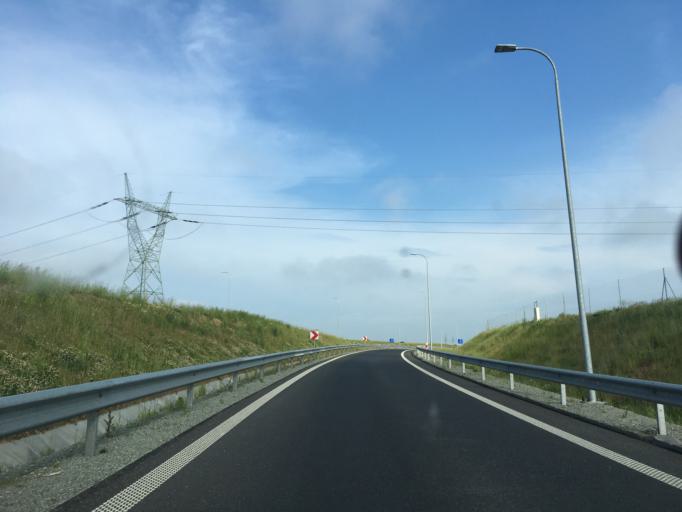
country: PL
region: West Pomeranian Voivodeship
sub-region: Koszalin
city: Koszalin
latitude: 54.1889
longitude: 16.1187
